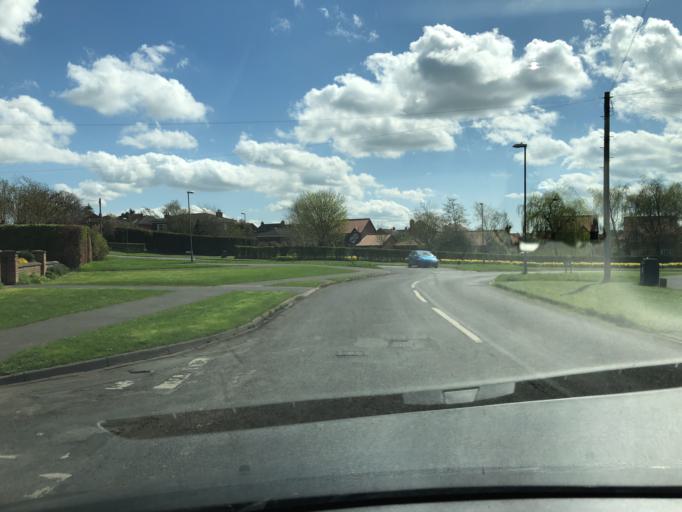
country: GB
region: England
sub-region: North Yorkshire
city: Northallerton
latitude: 54.3331
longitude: -1.4240
